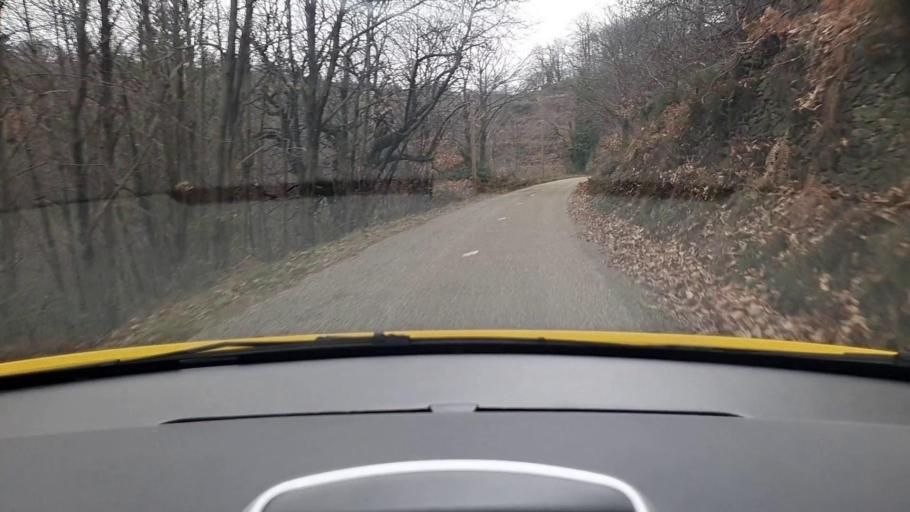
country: FR
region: Languedoc-Roussillon
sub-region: Departement du Gard
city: Besseges
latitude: 44.3652
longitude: 4.0260
